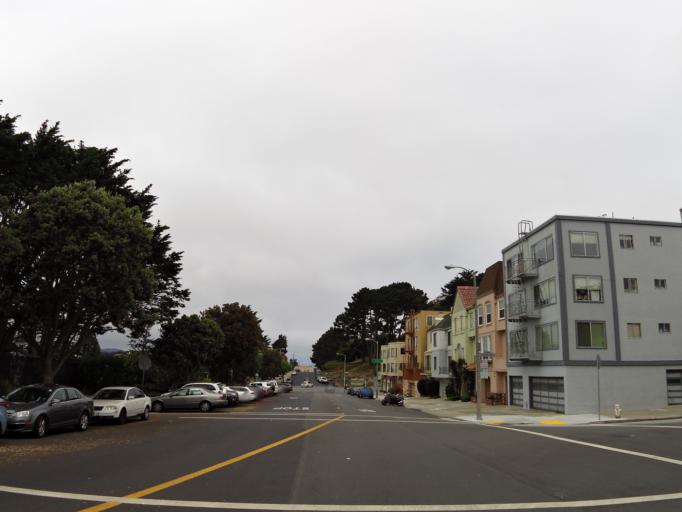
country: US
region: California
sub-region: San Francisco County
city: San Francisco
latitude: 37.7767
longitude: -122.4532
